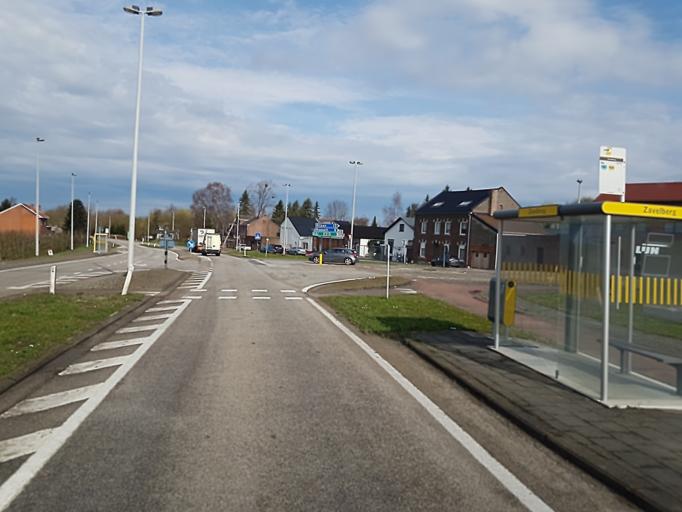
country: BE
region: Flanders
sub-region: Provincie Limburg
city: Tongeren
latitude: 50.7986
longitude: 5.4474
